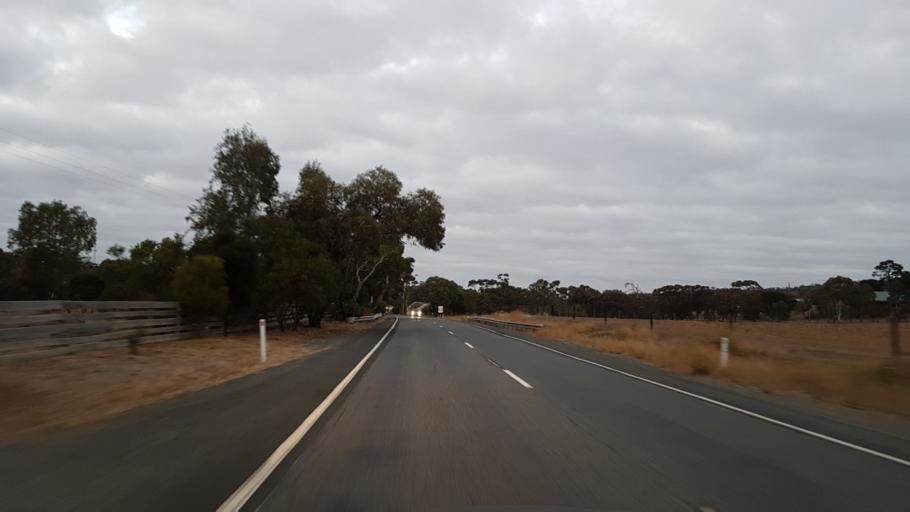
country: AU
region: South Australia
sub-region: Mount Barker
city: Callington
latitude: -35.0653
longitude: 139.0124
